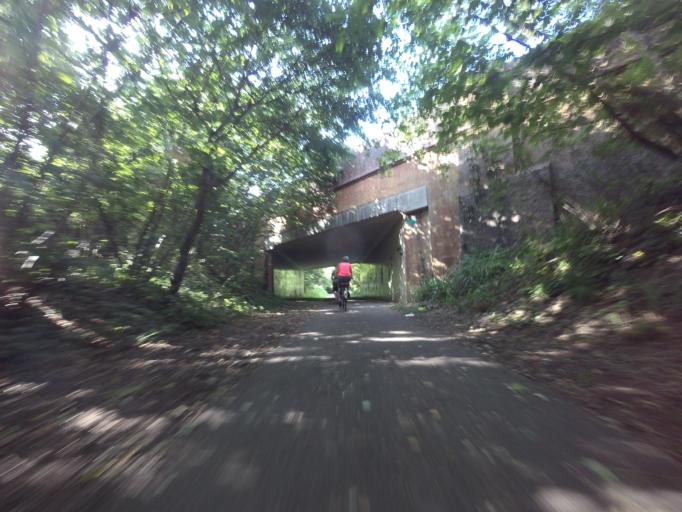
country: GB
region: England
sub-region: East Sussex
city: Hailsham
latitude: 50.8658
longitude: 0.2548
